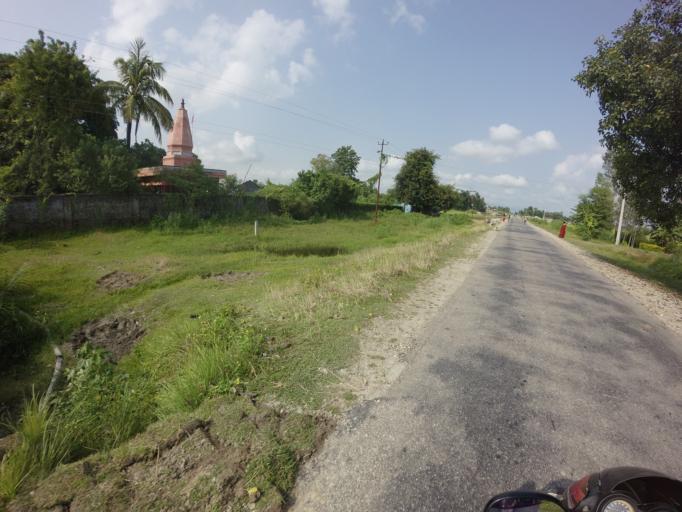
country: NP
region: Far Western
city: Tikapur
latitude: 28.4773
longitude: 81.0757
